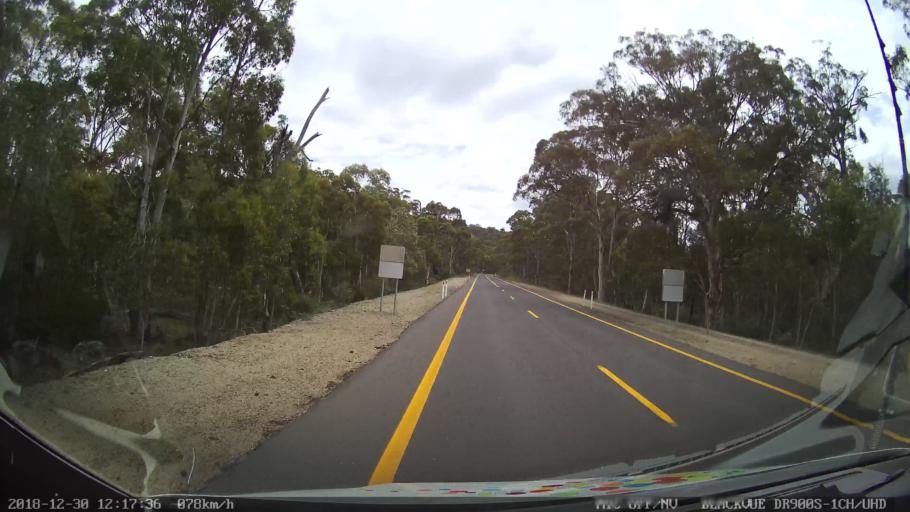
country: AU
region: New South Wales
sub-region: Snowy River
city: Jindabyne
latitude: -36.3532
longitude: 148.5581
